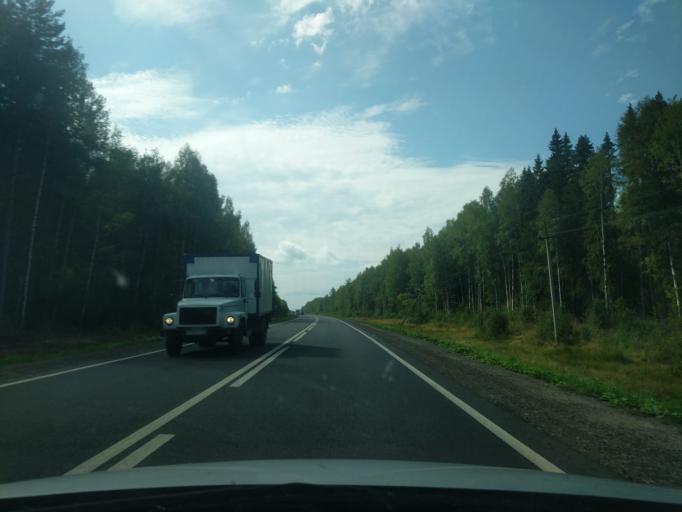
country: RU
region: Kostroma
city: Kadyy
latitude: 57.8199
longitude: 43.2403
